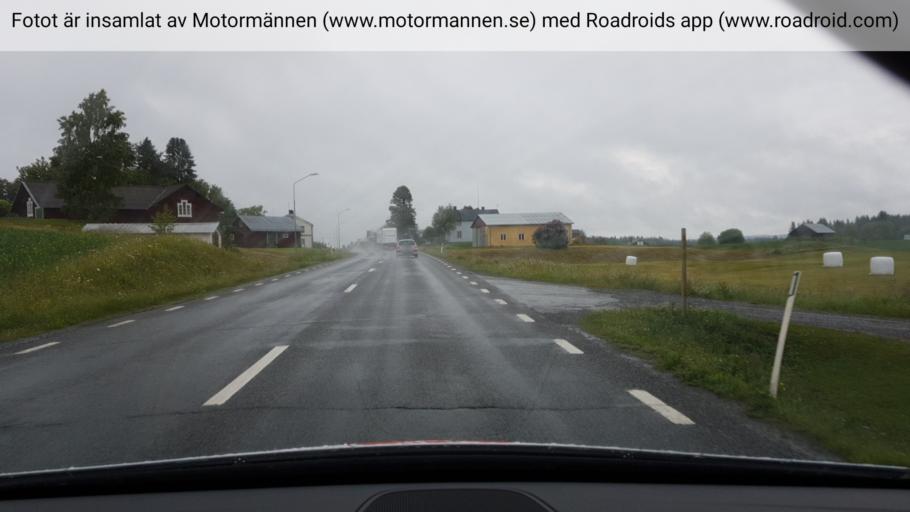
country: SE
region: Jaemtland
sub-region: OEstersunds Kommun
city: Lit
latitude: 63.4928
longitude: 15.2483
